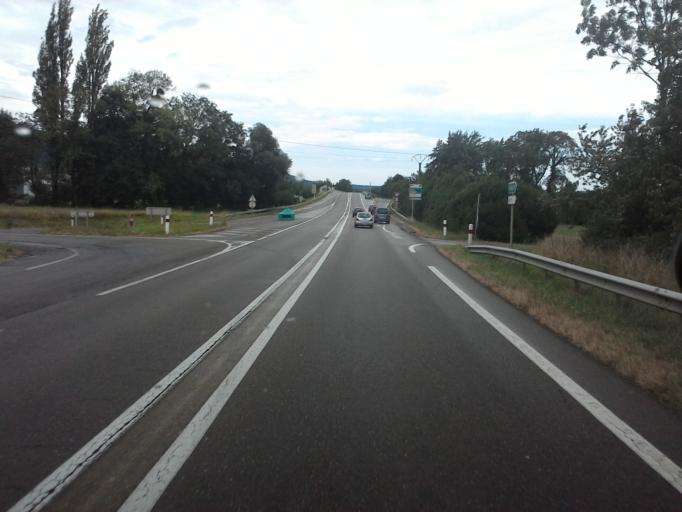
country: FR
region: Franche-Comte
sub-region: Departement du Jura
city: Poligny
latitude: 46.8469
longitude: 5.7040
